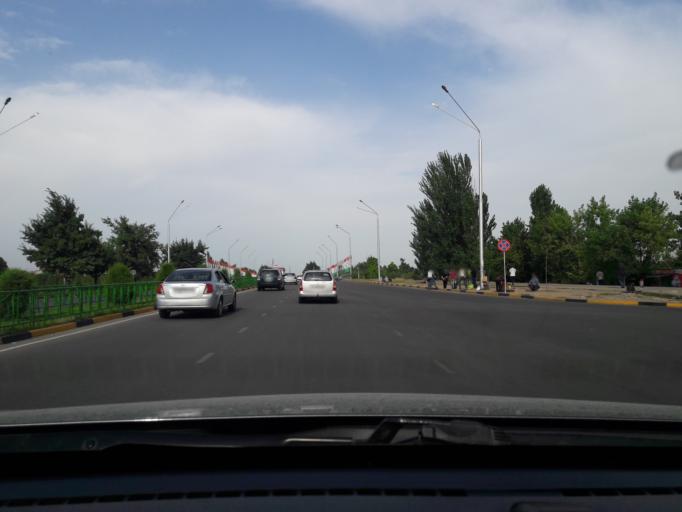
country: TJ
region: Dushanbe
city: Dushanbe
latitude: 38.5404
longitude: 68.7655
